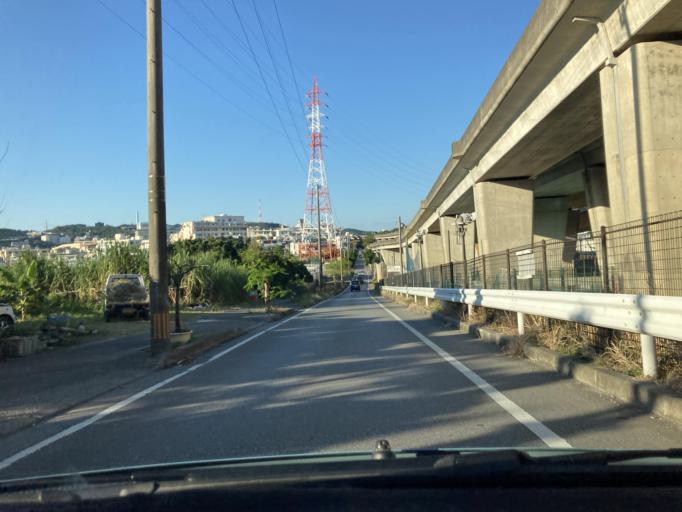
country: JP
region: Okinawa
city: Tomigusuku
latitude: 26.1949
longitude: 127.7395
